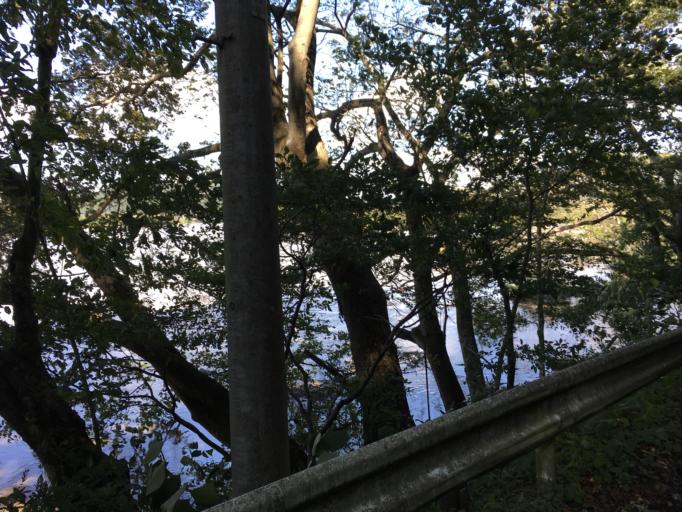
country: JP
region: Iwate
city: Ichinoseki
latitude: 38.8299
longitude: 141.2605
